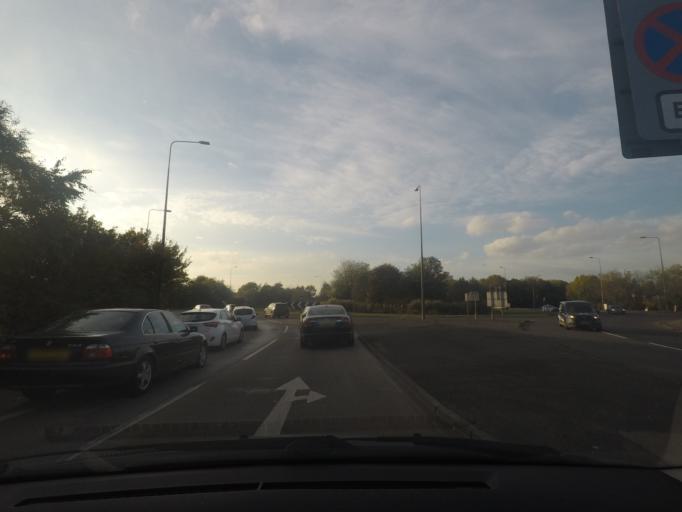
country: GB
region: England
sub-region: North East Lincolnshire
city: Grimbsy
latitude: 53.5778
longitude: -0.1080
